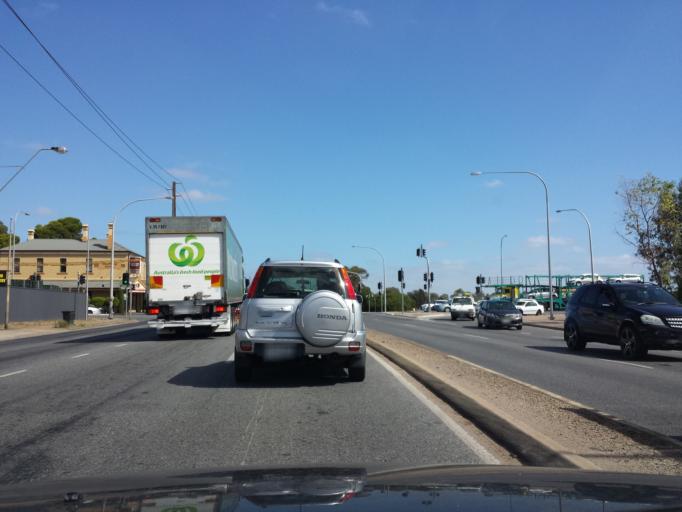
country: AU
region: South Australia
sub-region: Prospect
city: Prospect
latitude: -34.8738
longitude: 138.5841
